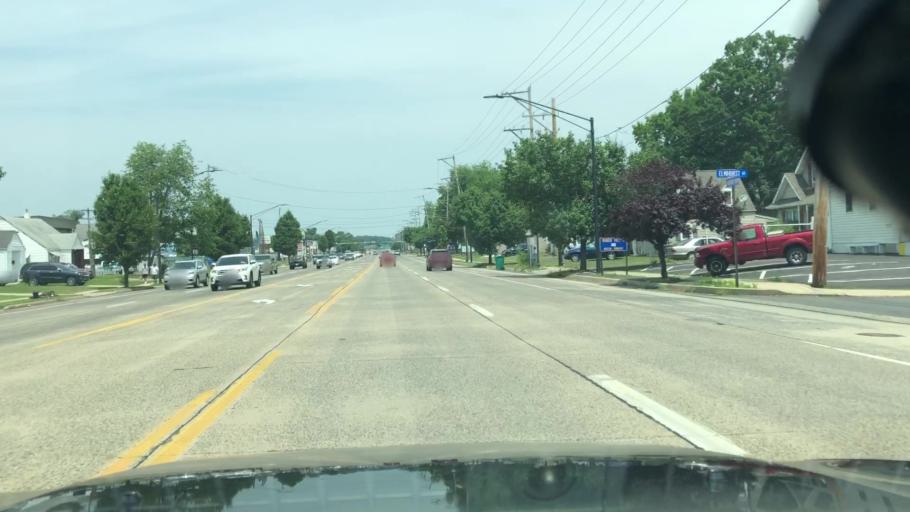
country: US
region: Pennsylvania
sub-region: Bucks County
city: Bristol
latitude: 40.1040
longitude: -74.8755
